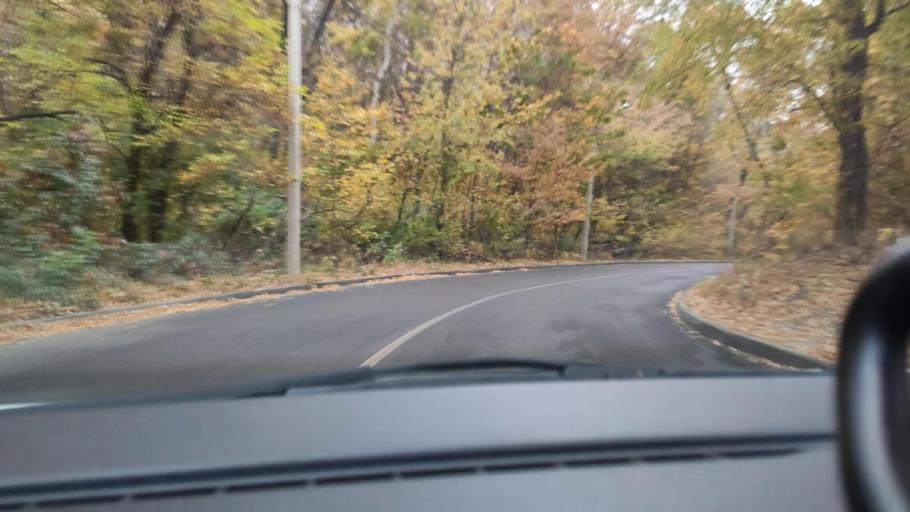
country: RU
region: Voronezj
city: Voronezh
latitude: 51.7188
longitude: 39.2352
